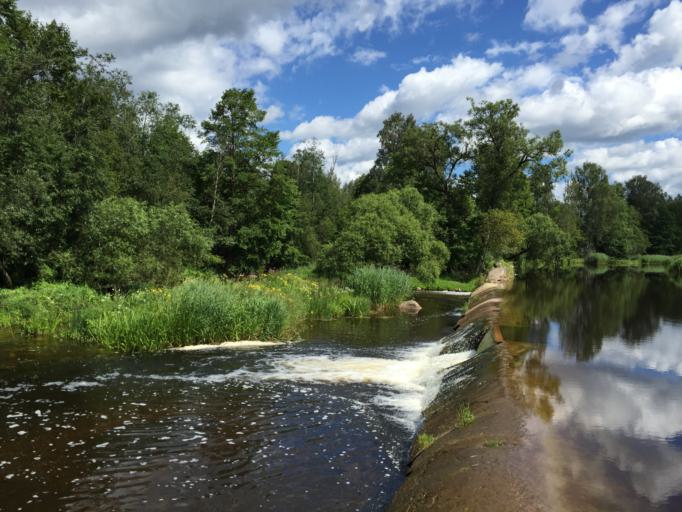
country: LV
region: Ropazu
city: Ropazi
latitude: 56.9753
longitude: 24.6477
